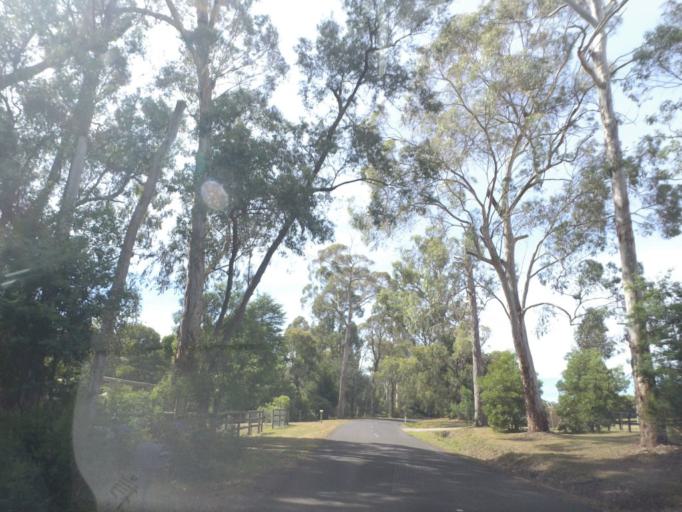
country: AU
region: Victoria
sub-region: Murrindindi
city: Kinglake West
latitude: -37.4558
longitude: 145.4182
